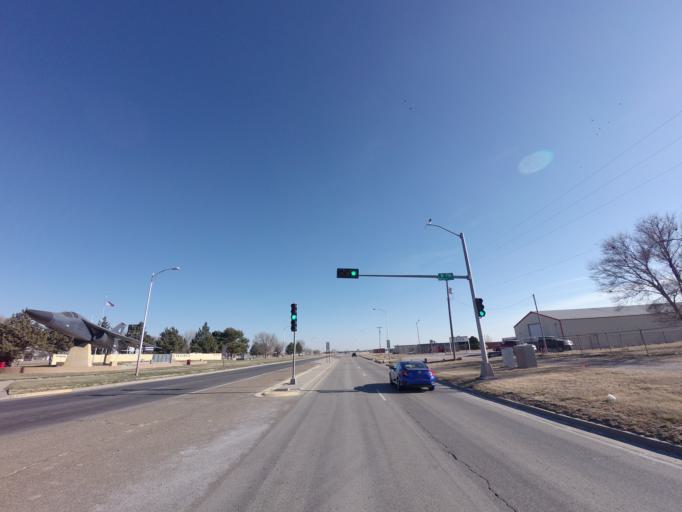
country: US
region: New Mexico
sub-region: Curry County
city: Clovis
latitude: 34.4039
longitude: -103.2464
